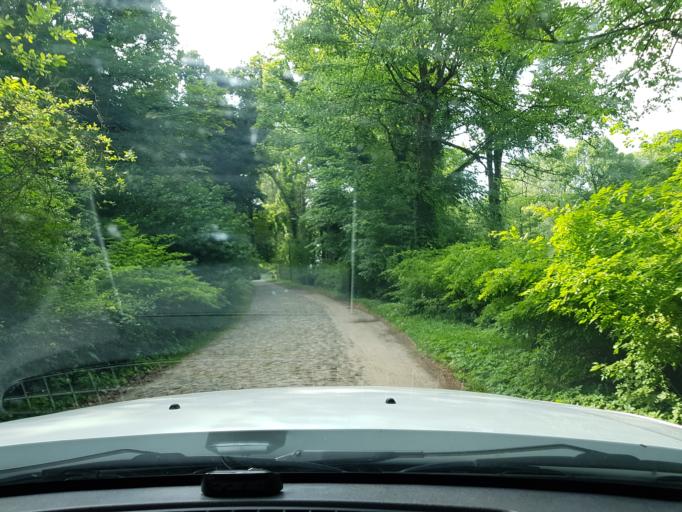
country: PL
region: West Pomeranian Voivodeship
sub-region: Powiat gryfinski
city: Chojna
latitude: 52.9967
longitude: 14.4858
